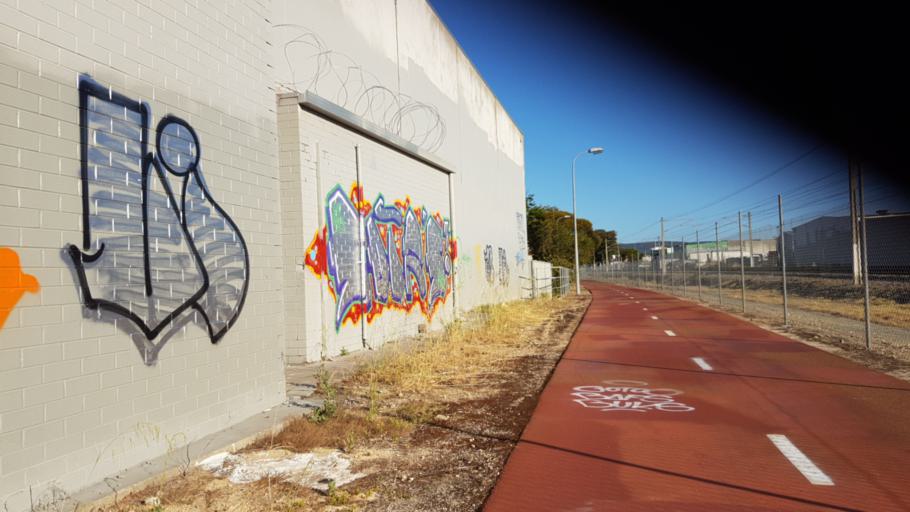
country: AU
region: Western Australia
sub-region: Gosnells
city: Maddington
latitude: -32.0469
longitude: 115.9789
